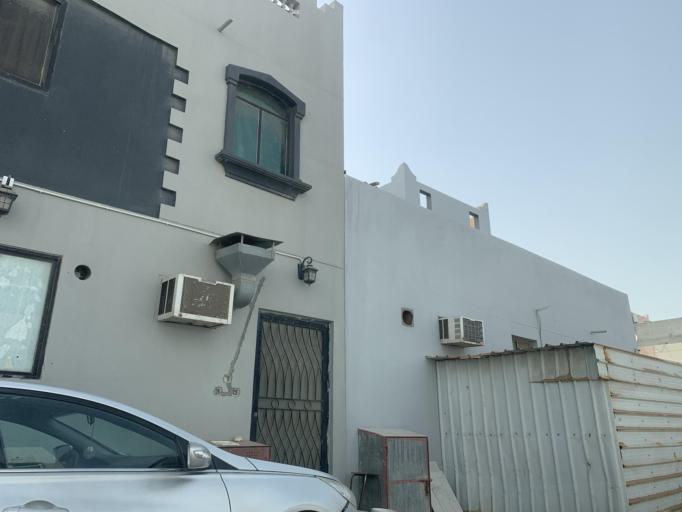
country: BH
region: Northern
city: Madinat `Isa
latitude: 26.1772
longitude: 50.5245
